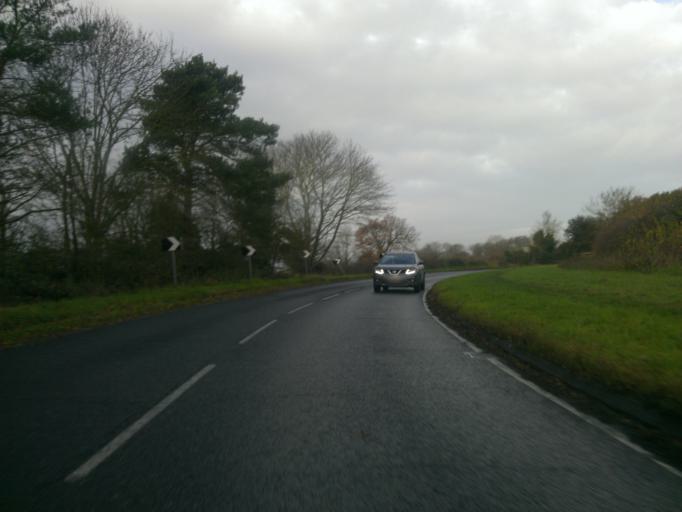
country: GB
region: England
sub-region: Essex
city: Wivenhoe
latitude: 51.8534
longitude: 0.9789
